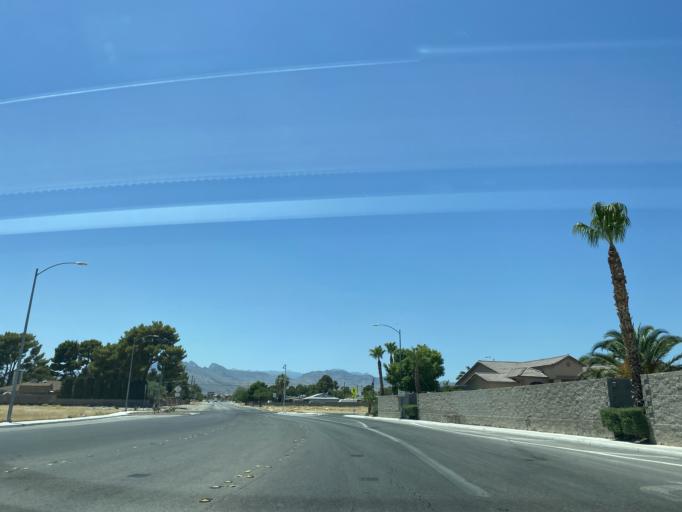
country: US
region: Nevada
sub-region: Clark County
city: Las Vegas
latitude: 36.2319
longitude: -115.2155
